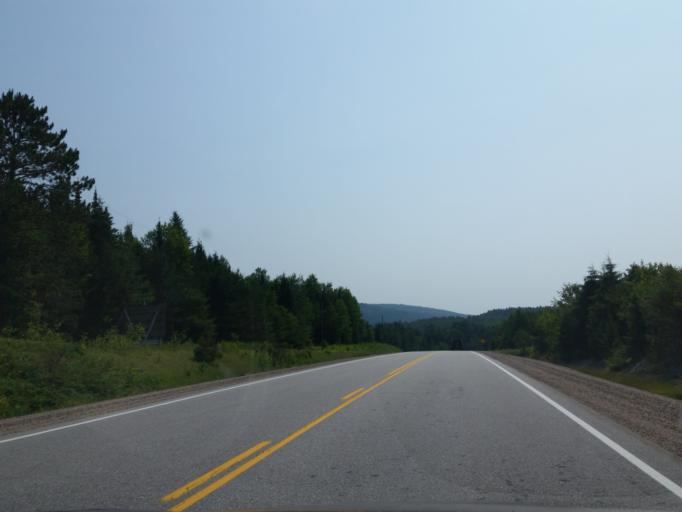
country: CA
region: Ontario
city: Mattawa
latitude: 46.3047
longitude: -78.5793
